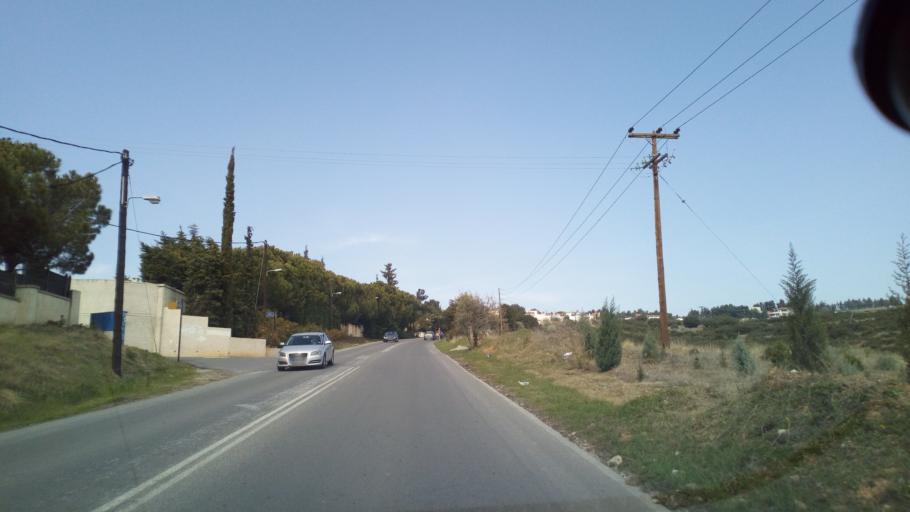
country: GR
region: Central Macedonia
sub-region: Nomos Thessalonikis
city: Panorama
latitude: 40.5720
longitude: 23.0251
